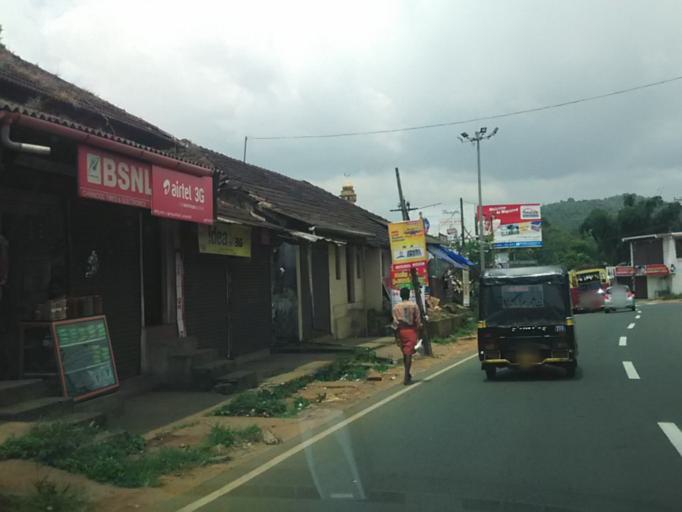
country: IN
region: Kerala
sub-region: Wayanad
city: Kalpetta
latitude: 11.5523
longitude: 76.0388
